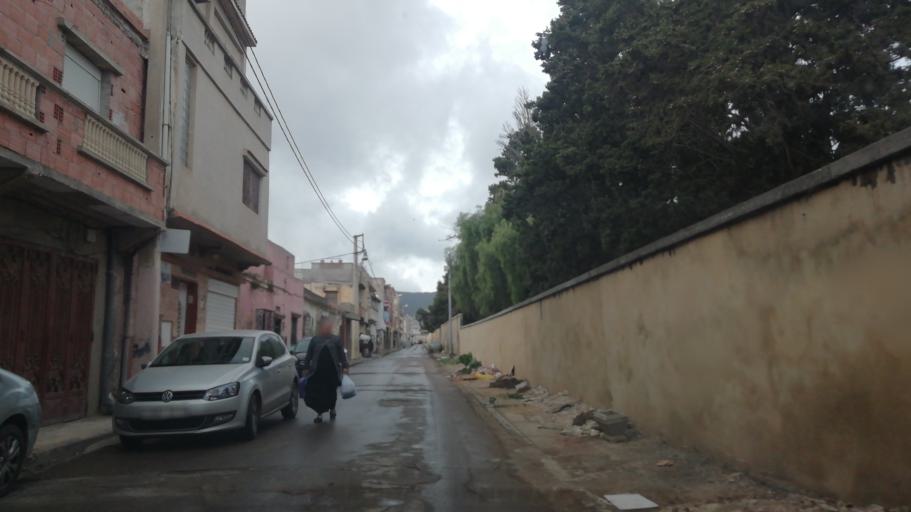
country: DZ
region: Oran
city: Oran
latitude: 35.6899
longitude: -0.6365
